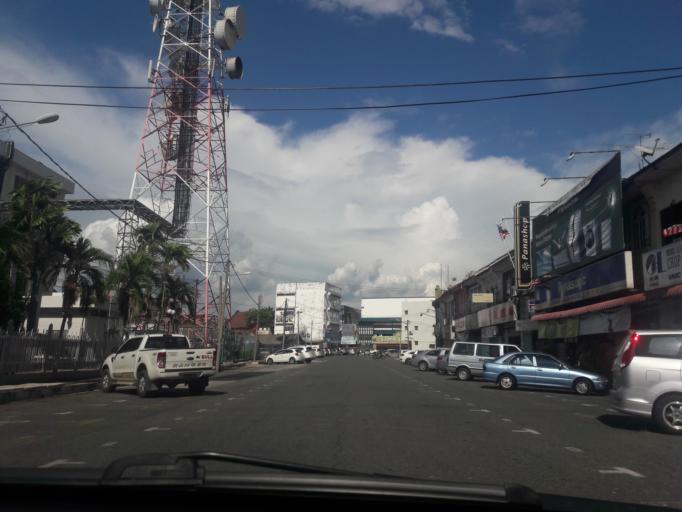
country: MY
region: Kedah
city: Sungai Petani
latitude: 5.6405
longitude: 100.4857
